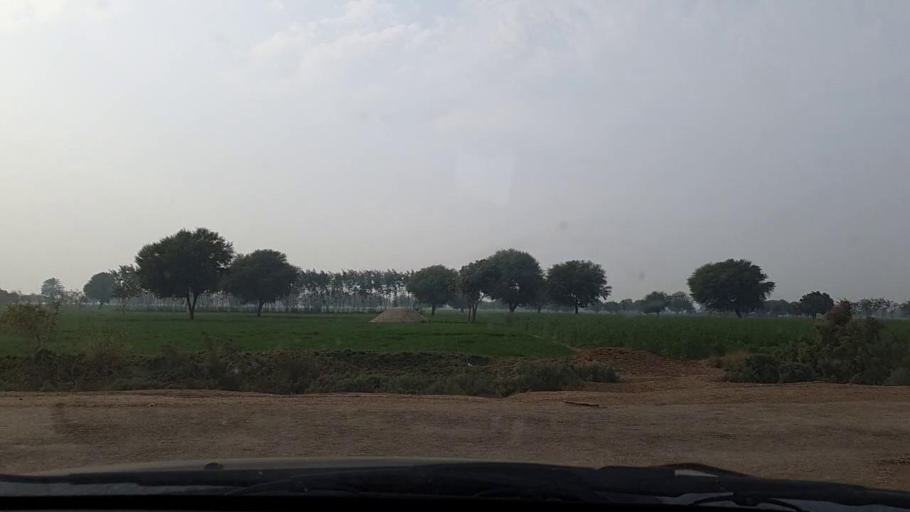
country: PK
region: Sindh
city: Pithoro
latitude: 25.7609
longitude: 69.3884
